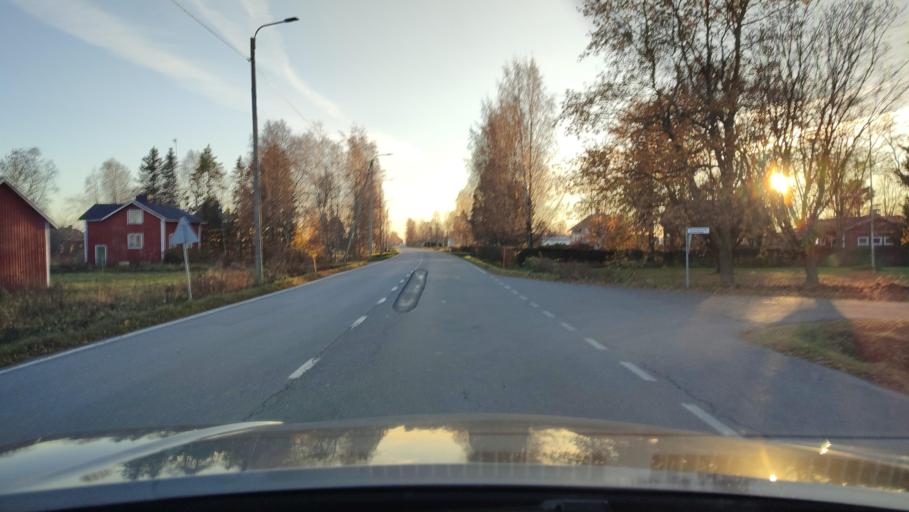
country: FI
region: Ostrobothnia
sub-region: Sydosterbotten
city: Naerpes
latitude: 62.6044
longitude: 21.4587
